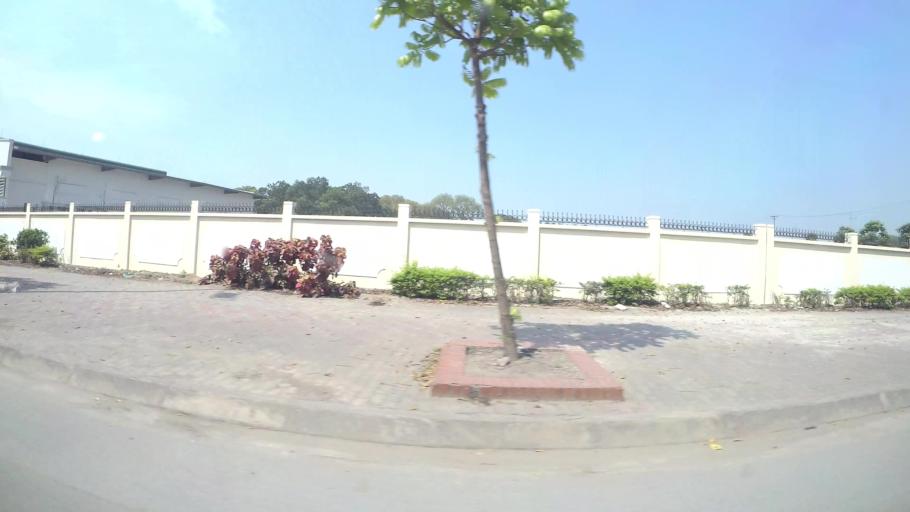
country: VN
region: Ha Noi
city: Hoan Kiem
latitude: 21.0688
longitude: 105.8794
